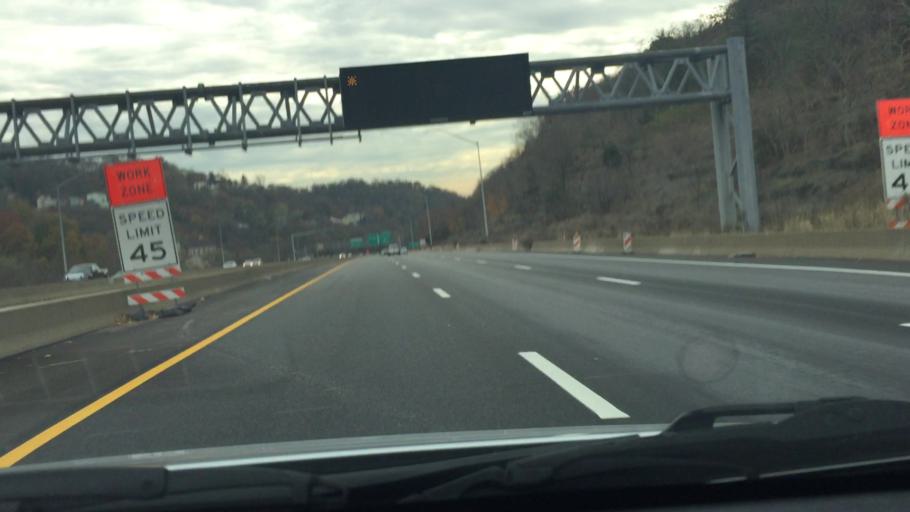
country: US
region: Pennsylvania
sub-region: Allegheny County
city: Millvale
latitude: 40.4707
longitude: -80.0039
